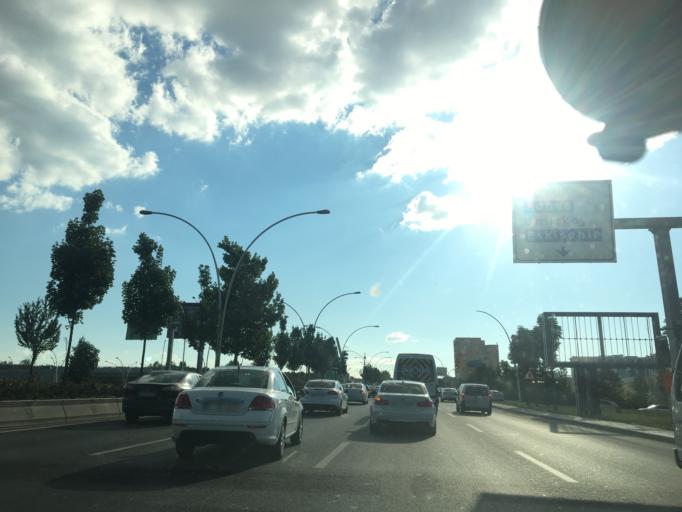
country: TR
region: Ankara
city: Ankara
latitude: 39.9088
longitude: 32.7878
